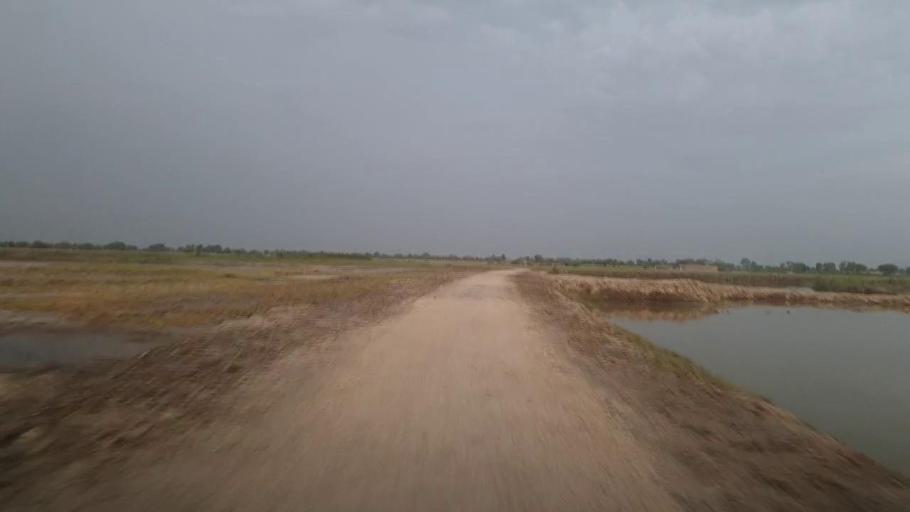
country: PK
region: Sindh
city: Karaundi
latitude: 27.0018
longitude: 68.3464
